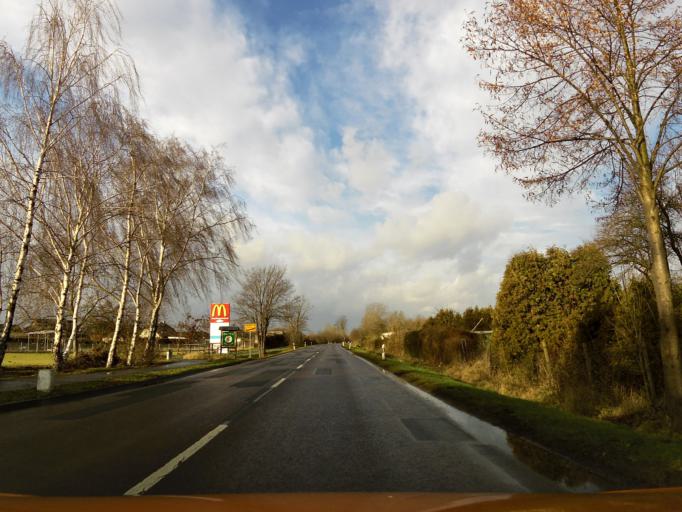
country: DE
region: Saxony-Anhalt
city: Ebendorf
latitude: 52.1860
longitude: 11.5706
